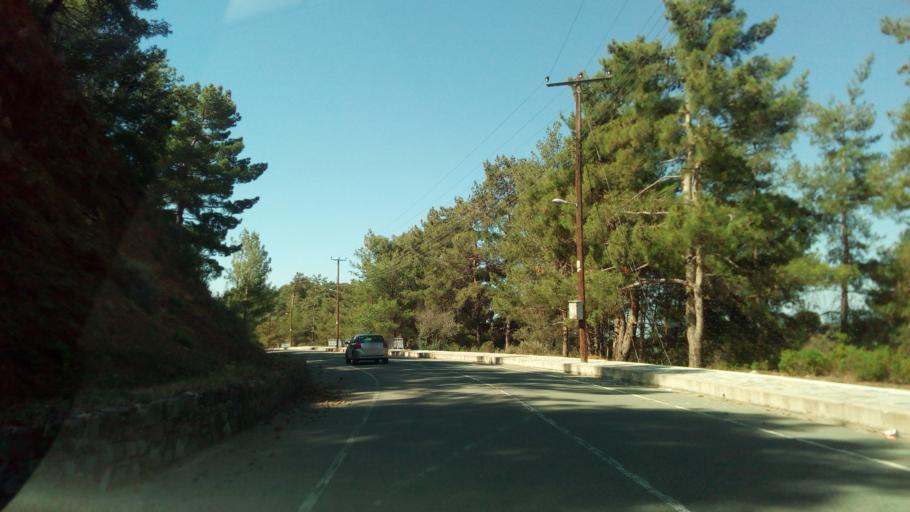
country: CY
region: Lefkosia
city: Lythrodontas
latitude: 34.8906
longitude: 33.2318
